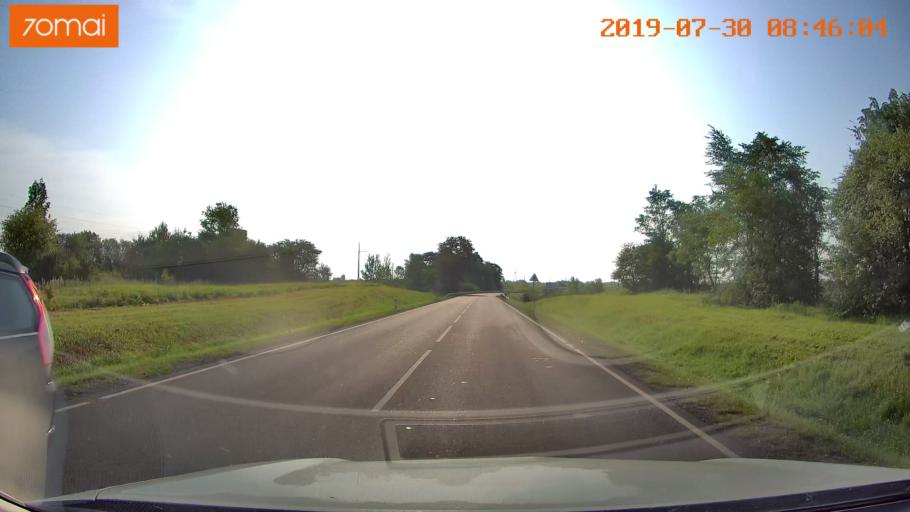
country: RU
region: Kaliningrad
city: Chernyakhovsk
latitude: 54.6250
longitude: 21.8768
